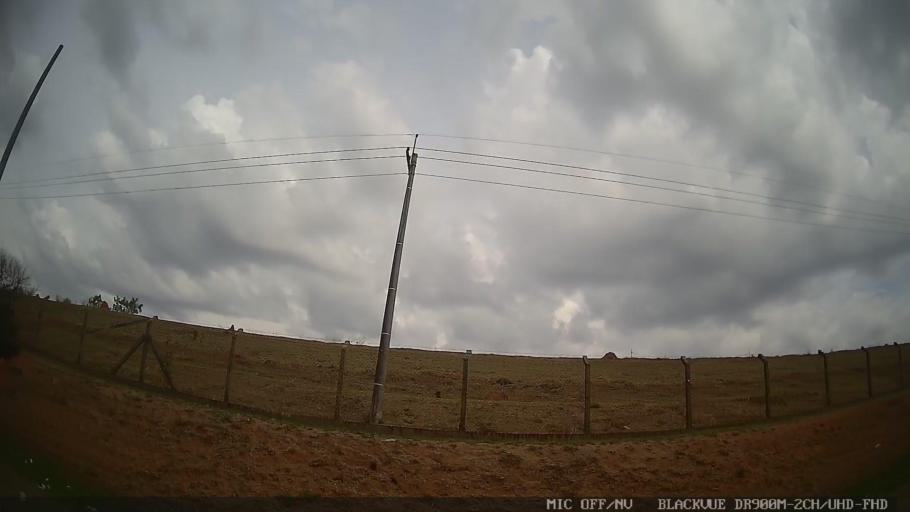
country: BR
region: Sao Paulo
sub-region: Indaiatuba
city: Indaiatuba
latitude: -23.1370
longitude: -47.2441
